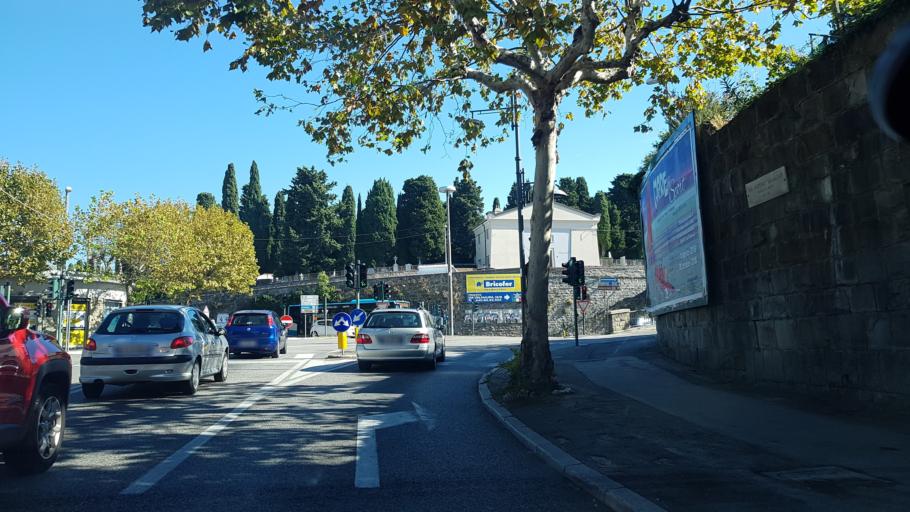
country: IT
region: Friuli Venezia Giulia
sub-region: Provincia di Trieste
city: Trieste
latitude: 45.6312
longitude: 13.7913
